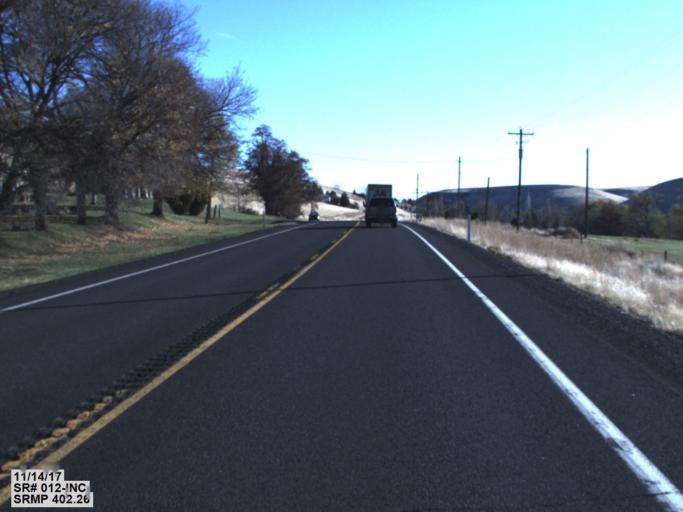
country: US
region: Washington
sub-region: Garfield County
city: Pomeroy
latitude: 46.4776
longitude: -117.6250
